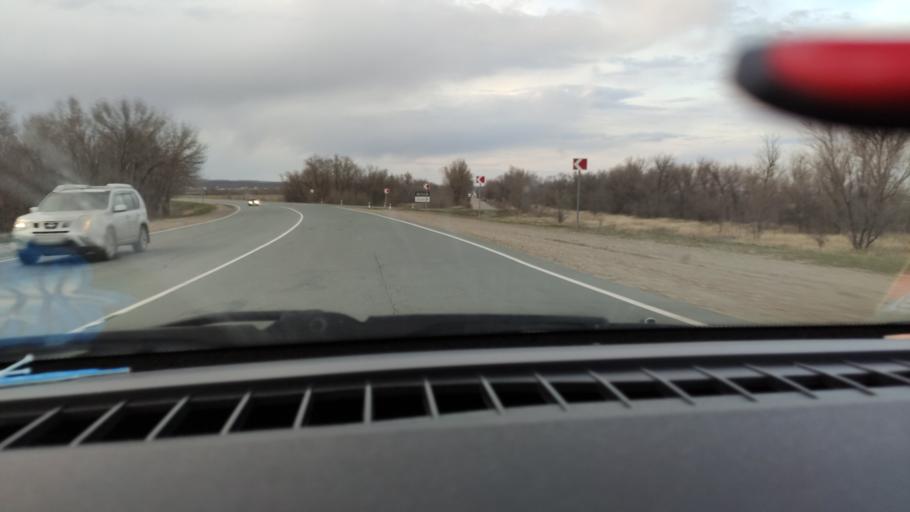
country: RU
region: Saratov
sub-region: Saratovskiy Rayon
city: Saratov
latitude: 51.7205
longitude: 46.0265
